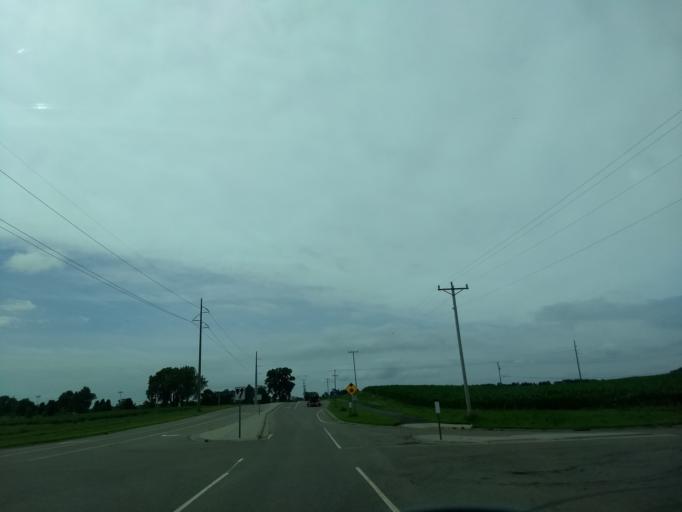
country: US
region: Minnesota
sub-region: Dakota County
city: Rosemount
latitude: 44.7413
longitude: -93.0857
